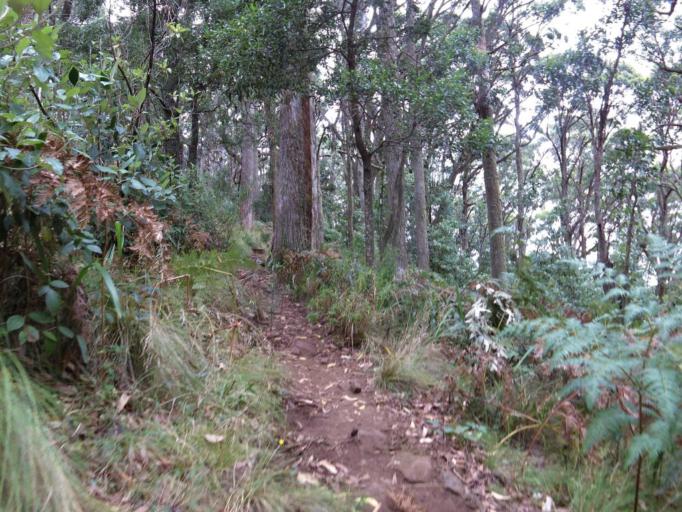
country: AU
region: Victoria
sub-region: Hume
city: Sunbury
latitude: -37.3938
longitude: 144.5753
